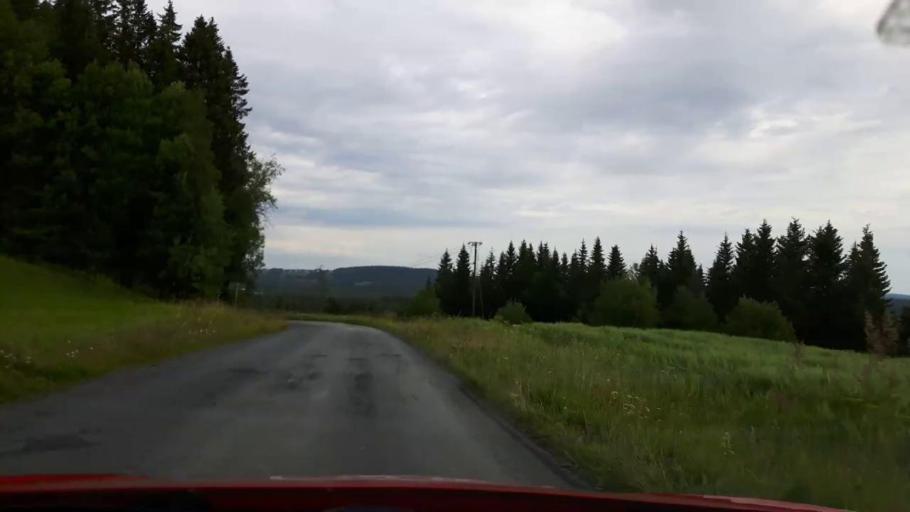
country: SE
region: Jaemtland
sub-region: Stroemsunds Kommun
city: Stroemsund
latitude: 63.5271
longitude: 15.3588
